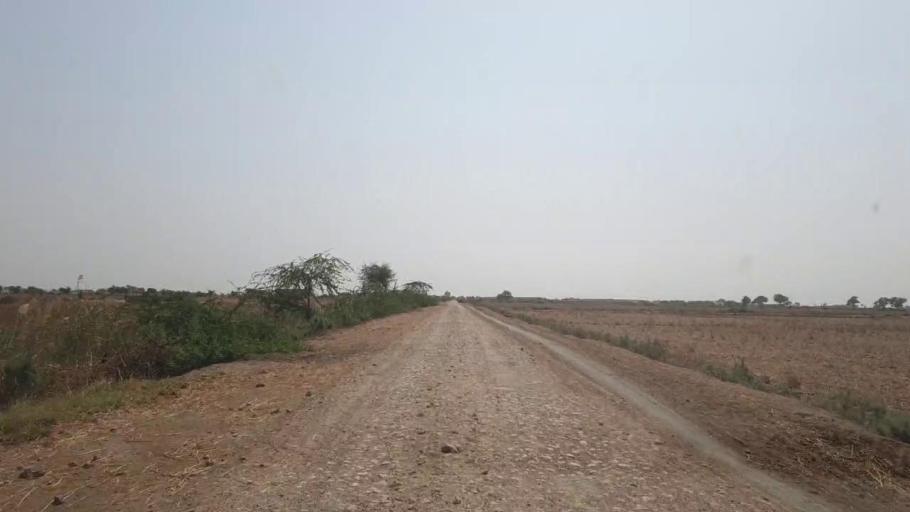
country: PK
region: Sindh
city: Jati
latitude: 24.4295
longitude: 68.5524
